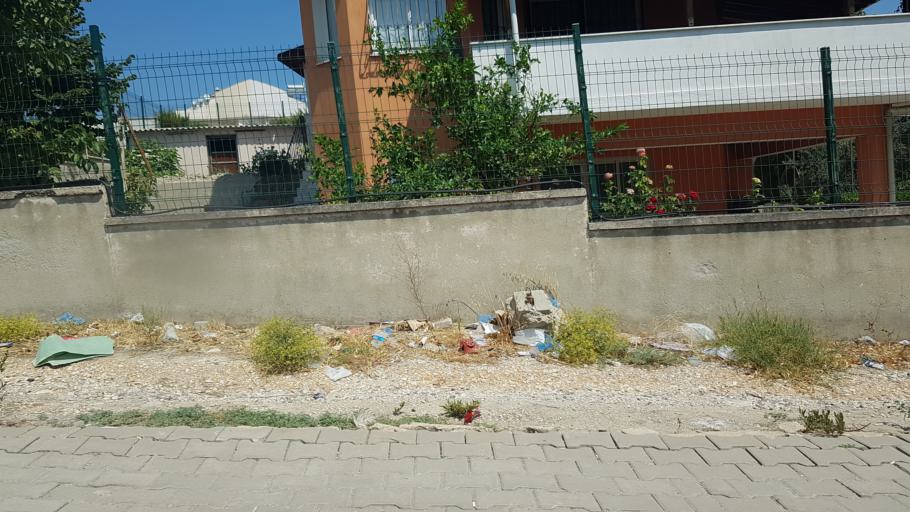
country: TR
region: Izmir
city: Urla
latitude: 38.3283
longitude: 26.7632
